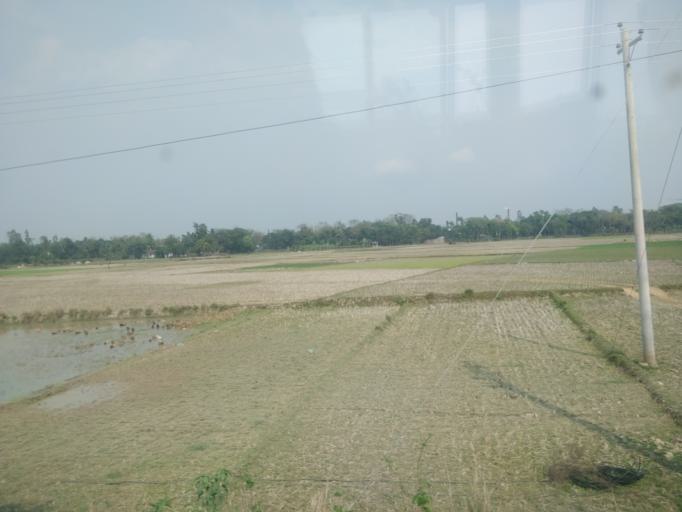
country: BD
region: Sylhet
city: Habiganj
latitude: 24.3186
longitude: 91.4355
